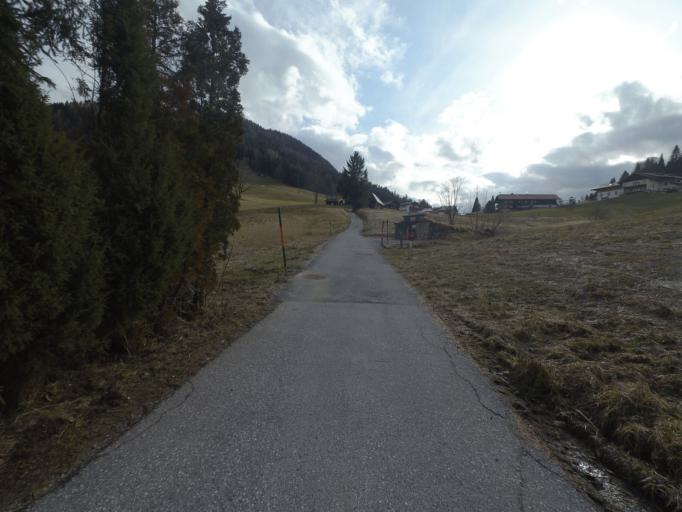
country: AT
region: Salzburg
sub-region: Politischer Bezirk Hallein
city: Hallein
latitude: 47.6583
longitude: 13.0868
